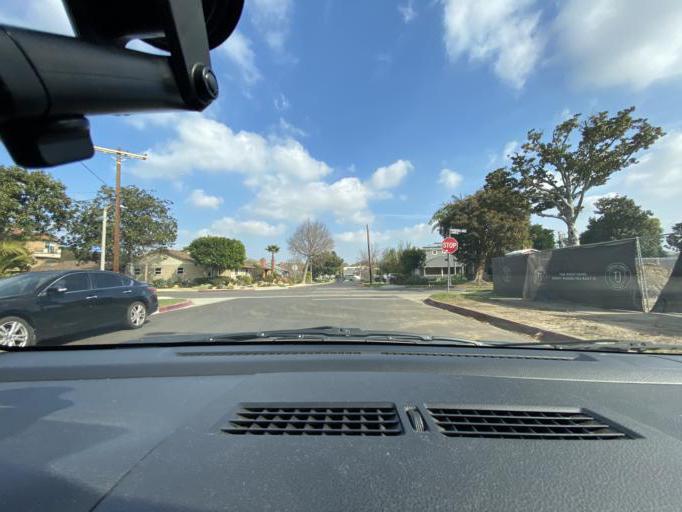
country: US
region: California
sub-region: Los Angeles County
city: Westwood, Los Angeles
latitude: 34.0228
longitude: -118.4362
